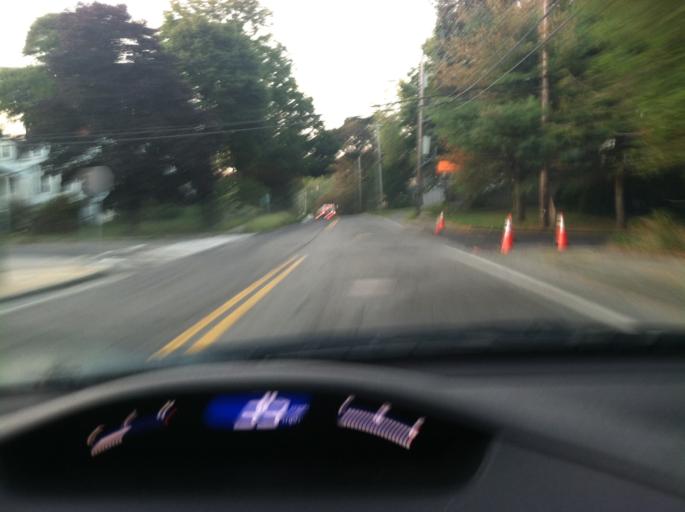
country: US
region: Massachusetts
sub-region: Middlesex County
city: Lexington
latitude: 42.4671
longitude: -71.2427
